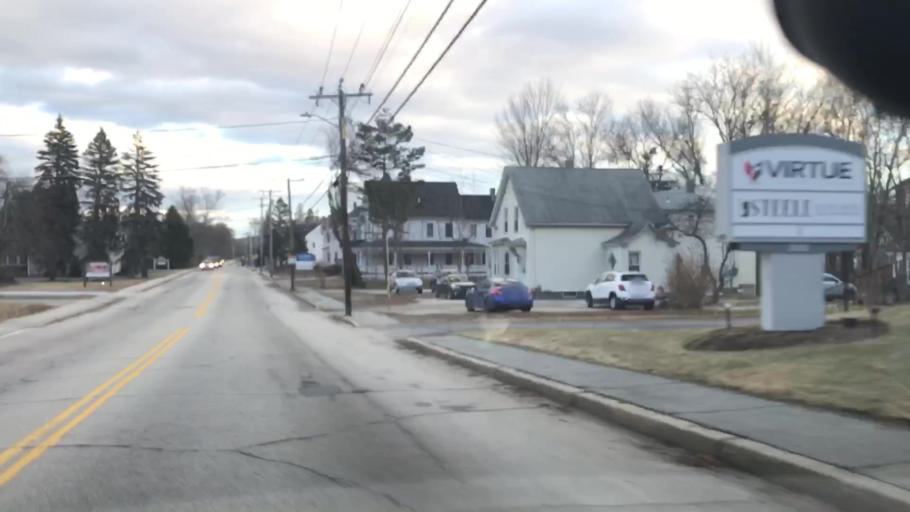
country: US
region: New Hampshire
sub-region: Hillsborough County
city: Milford
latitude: 42.8313
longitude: -71.6400
